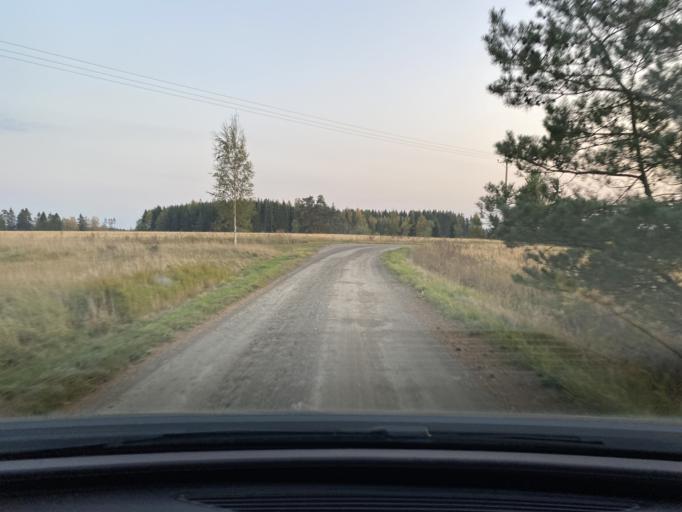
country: FI
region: Pirkanmaa
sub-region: Lounais-Pirkanmaa
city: Punkalaidun
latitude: 61.1083
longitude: 23.2239
